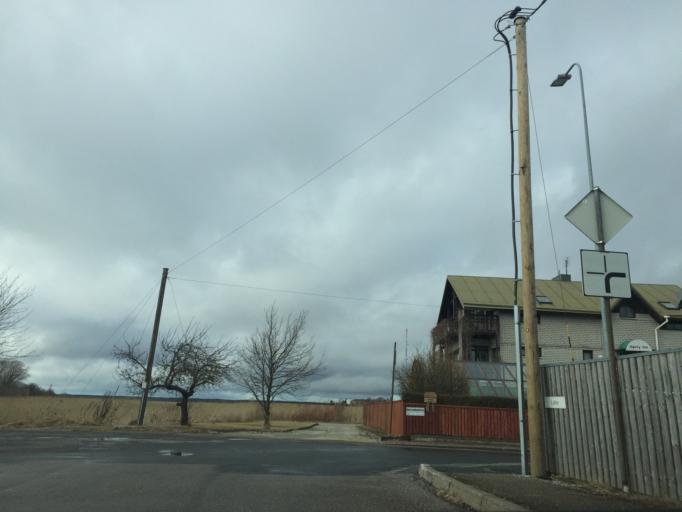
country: EE
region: Laeaene
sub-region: Haapsalu linn
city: Haapsalu
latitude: 58.9545
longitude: 23.5221
